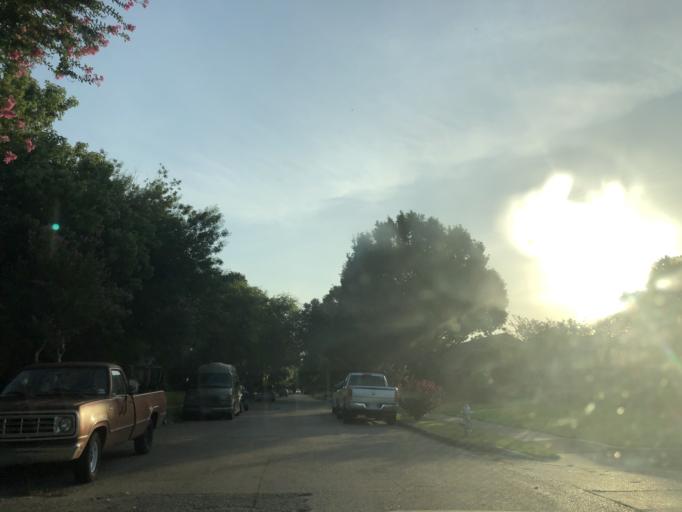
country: US
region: Texas
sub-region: Dallas County
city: Garland
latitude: 32.8574
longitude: -96.6306
